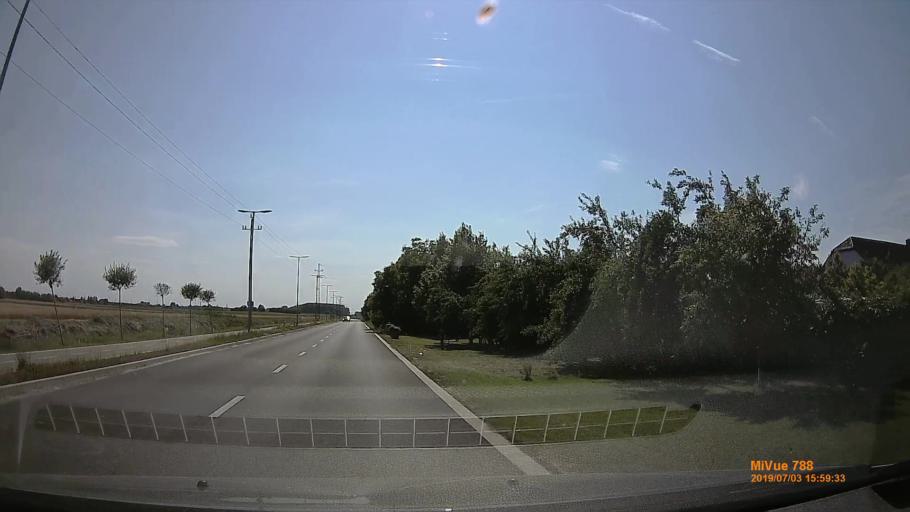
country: HU
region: Gyor-Moson-Sopron
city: Toltestava
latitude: 47.6976
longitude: 17.7304
